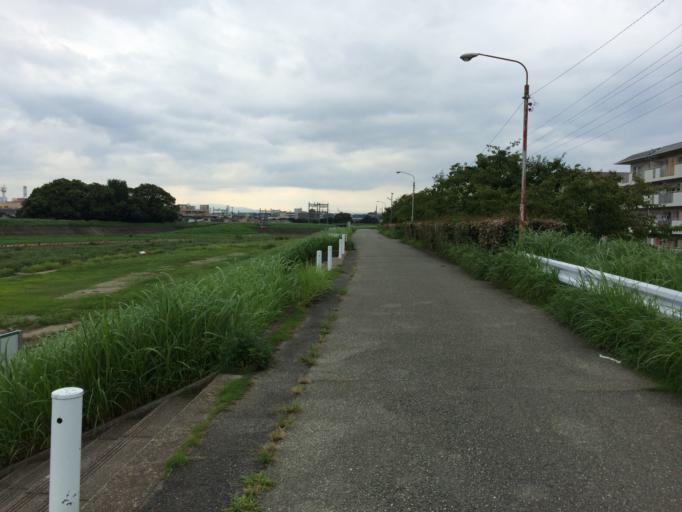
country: JP
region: Osaka
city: Ibaraki
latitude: 34.8217
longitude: 135.5839
